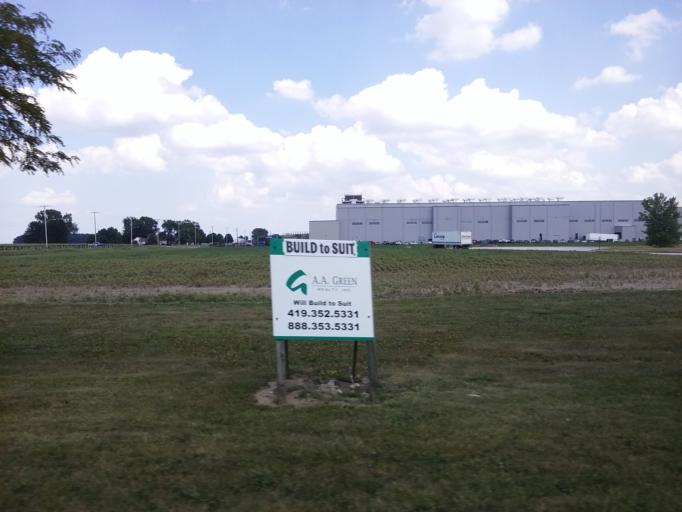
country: US
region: Ohio
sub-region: Wood County
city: Bowling Green
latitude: 41.3844
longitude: -83.6103
